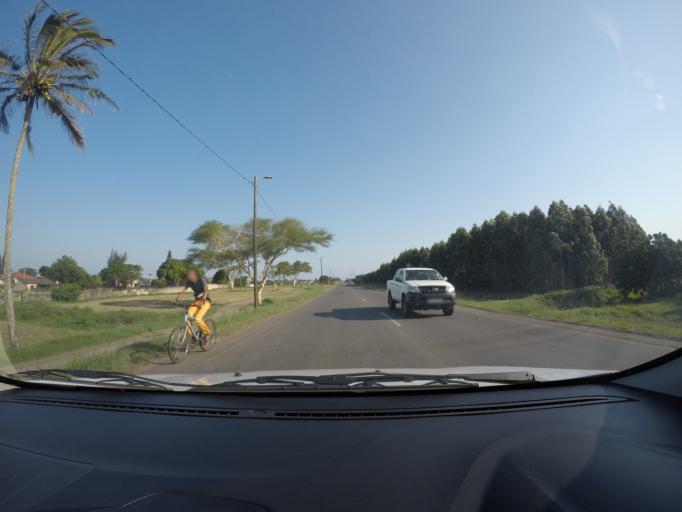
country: ZA
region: KwaZulu-Natal
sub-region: uThungulu District Municipality
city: Richards Bay
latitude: -28.7175
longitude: 32.0317
